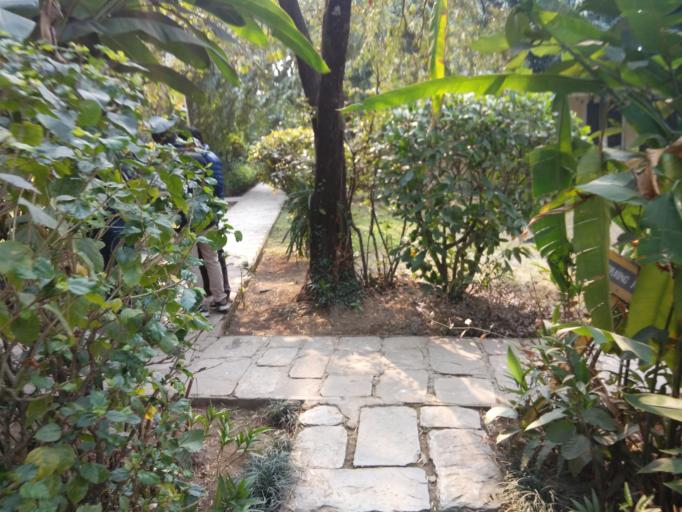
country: NP
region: Central Region
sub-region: Narayani Zone
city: Bharatpur
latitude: 27.6883
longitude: 84.4293
